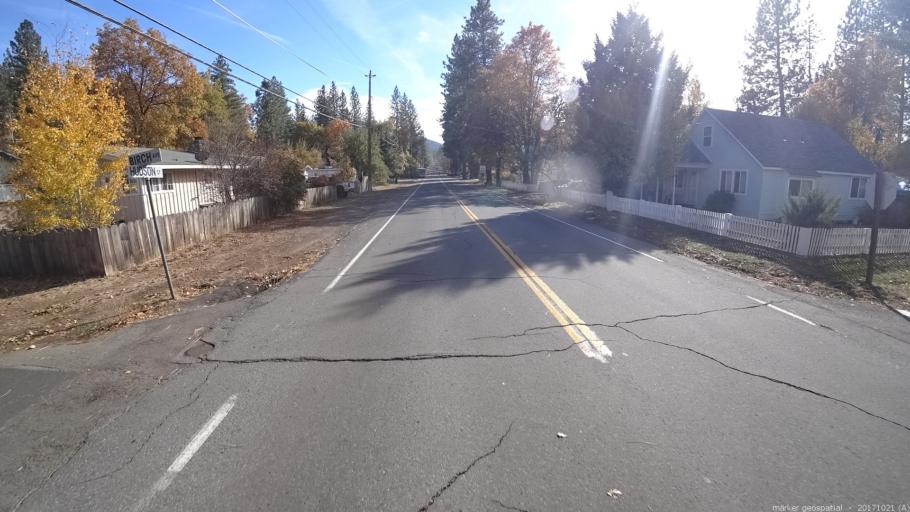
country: US
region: California
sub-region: Shasta County
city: Burney
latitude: 40.8794
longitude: -121.6614
